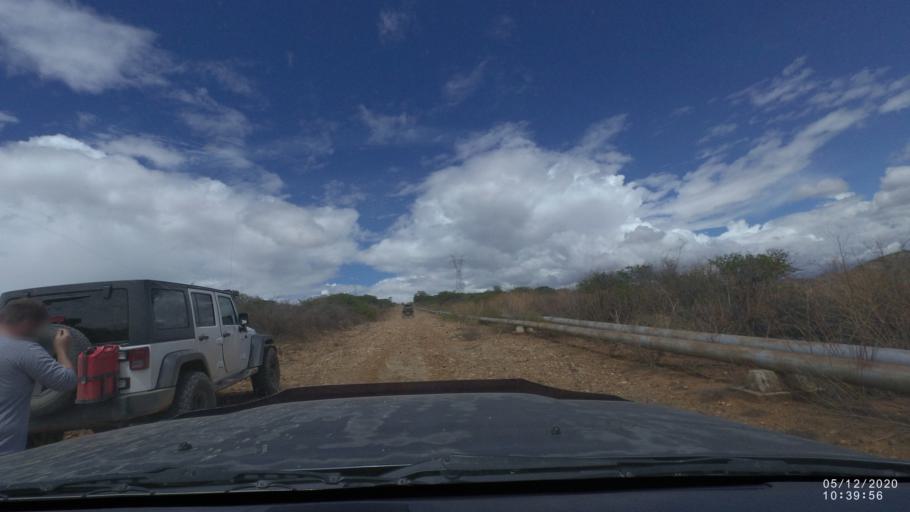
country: BO
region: Cochabamba
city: Sipe Sipe
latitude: -17.5457
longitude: -66.2850
